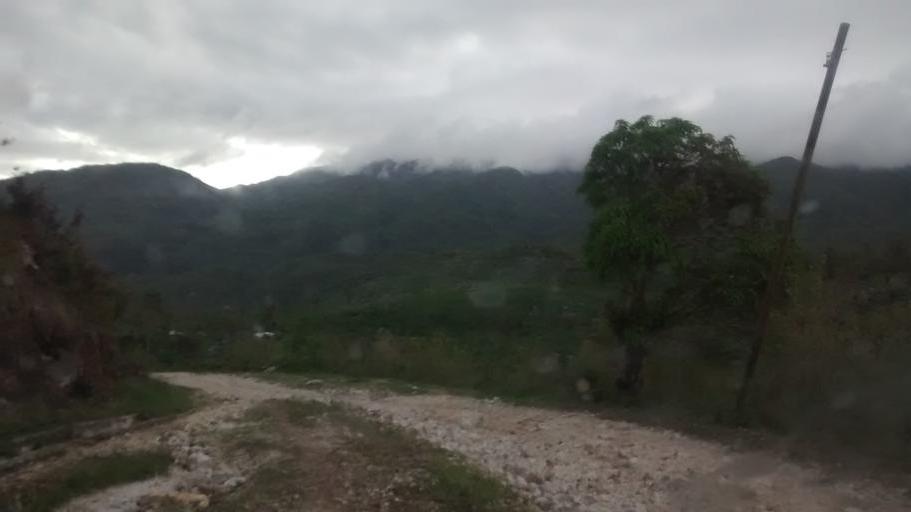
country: HT
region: Grandans
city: Corail
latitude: 18.4776
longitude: -73.7933
